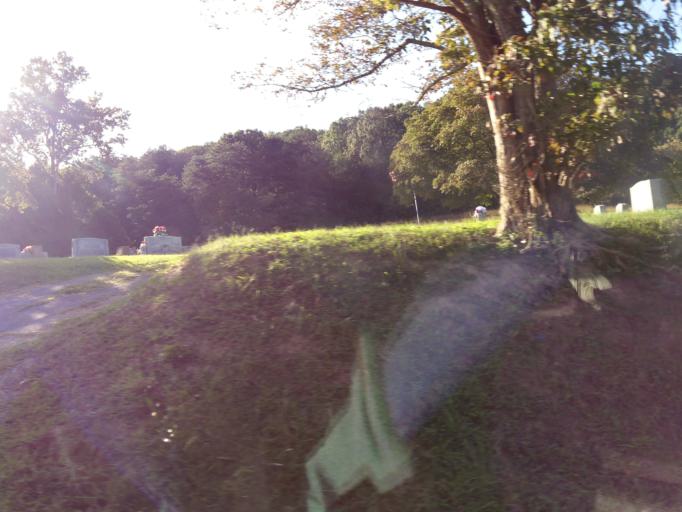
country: US
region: Tennessee
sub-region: Union County
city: Luttrell
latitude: 36.2411
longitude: -83.7463
